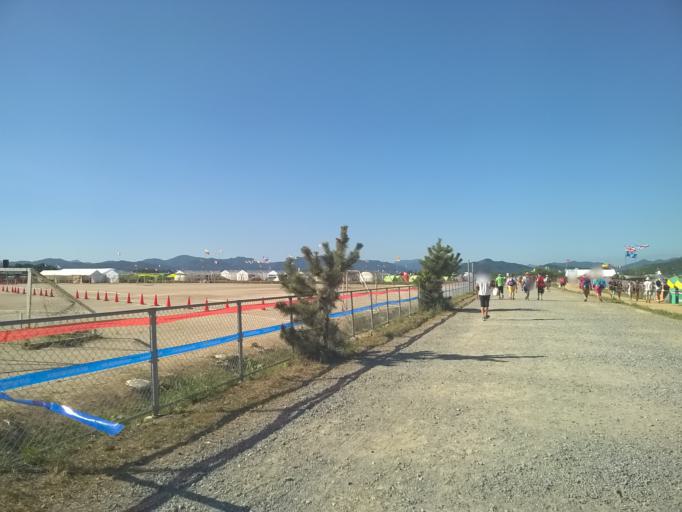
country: JP
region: Yamaguchi
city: Ogori-shimogo
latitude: 34.0187
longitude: 131.3725
